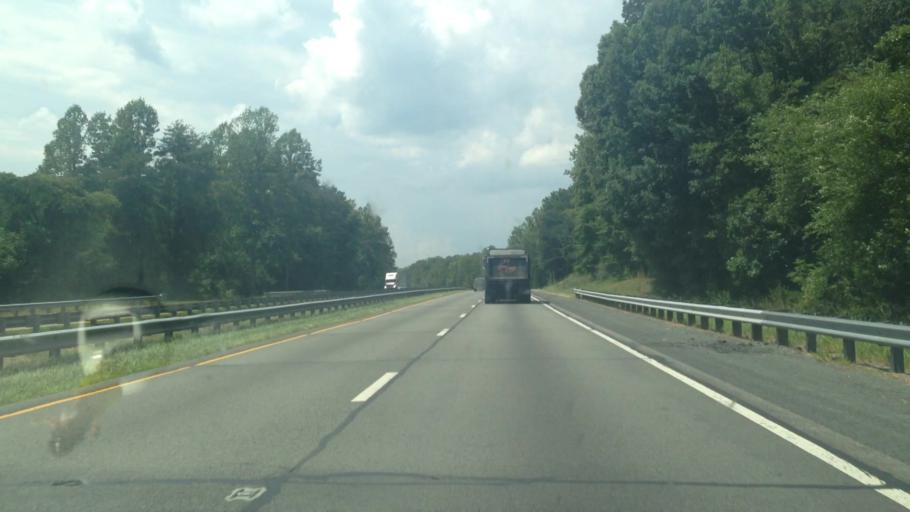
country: US
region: North Carolina
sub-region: Stokes County
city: King
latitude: 36.2947
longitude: -80.4065
